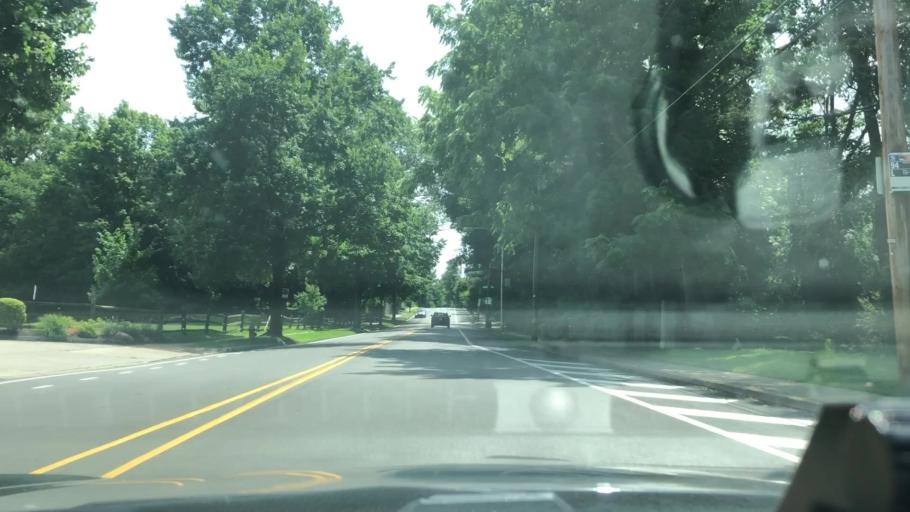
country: US
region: Pennsylvania
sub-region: Montgomery County
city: Flourtown
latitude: 40.0842
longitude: -75.2100
